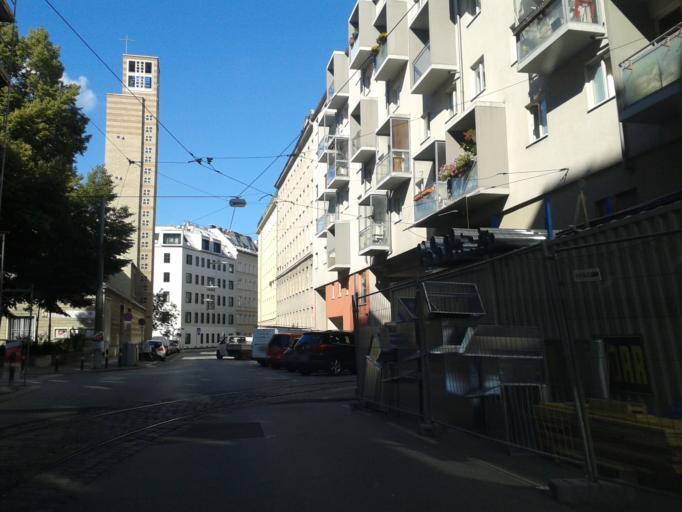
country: AT
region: Vienna
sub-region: Wien Stadt
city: Vienna
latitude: 48.1969
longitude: 16.4055
